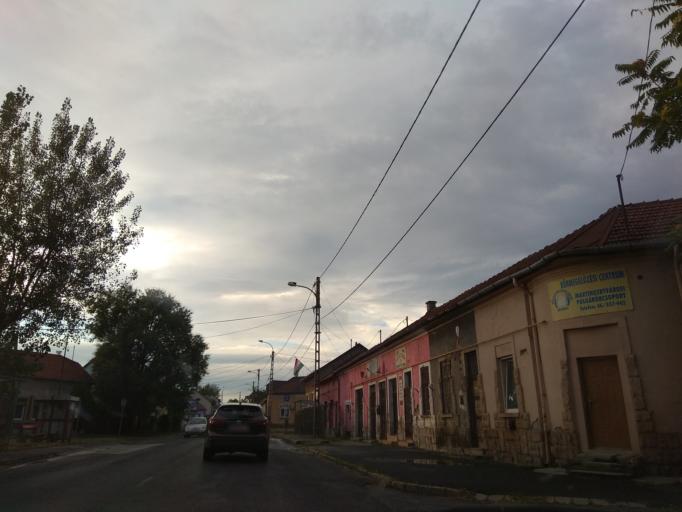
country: HU
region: Borsod-Abauj-Zemplen
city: Miskolc
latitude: 48.0947
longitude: 20.8048
